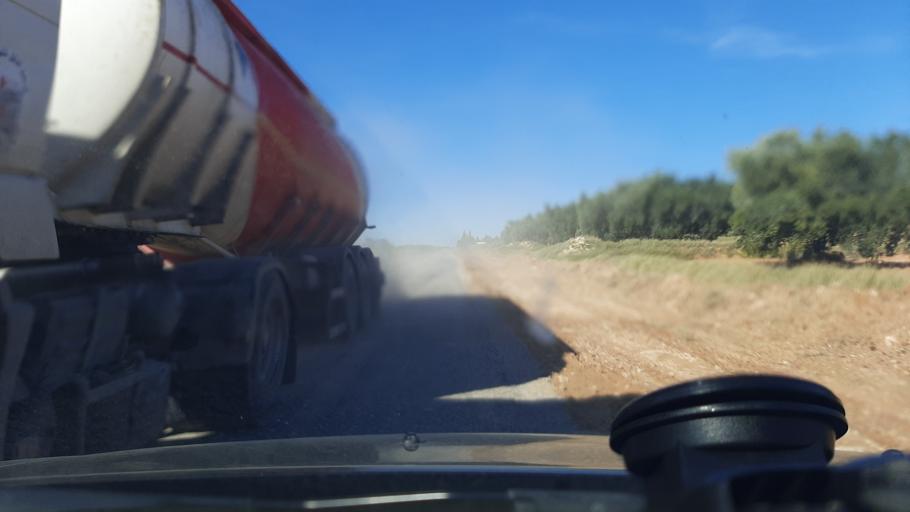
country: TN
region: Safaqis
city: Sfax
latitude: 34.9381
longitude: 10.5607
